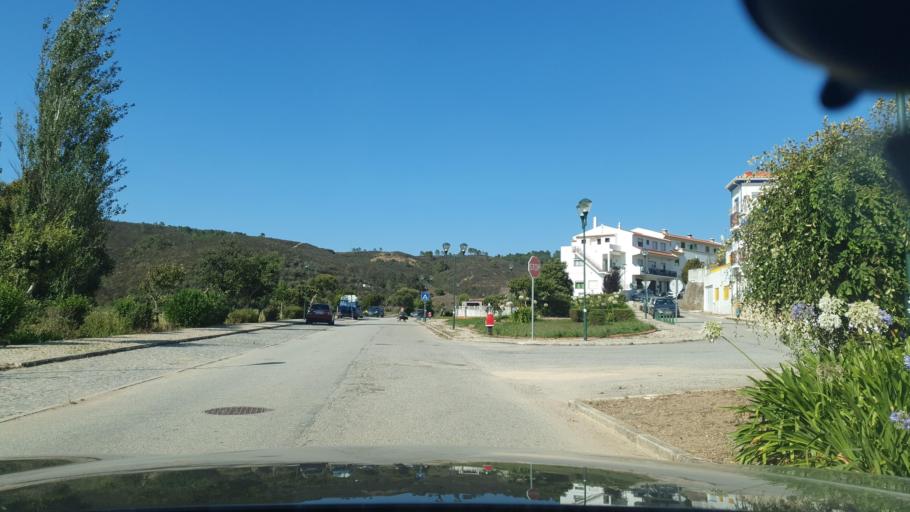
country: PT
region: Beja
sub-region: Odemira
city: Sao Teotonio
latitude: 37.4335
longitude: -8.7726
